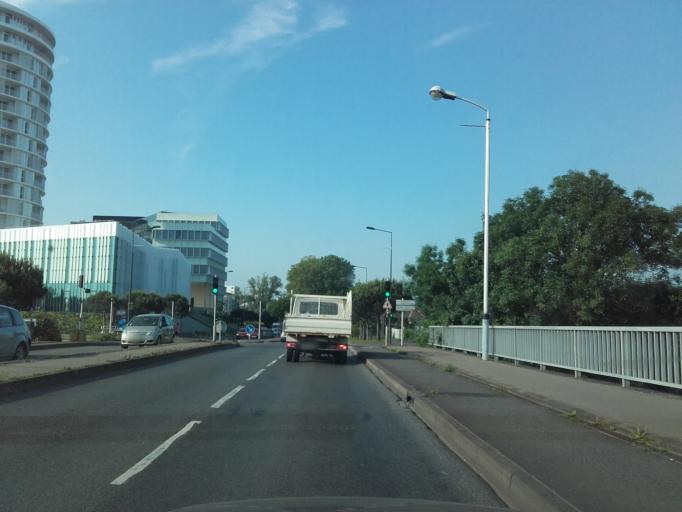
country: FR
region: Centre
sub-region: Departement d'Indre-et-Loire
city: Tours
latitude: 47.3721
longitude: 0.6781
